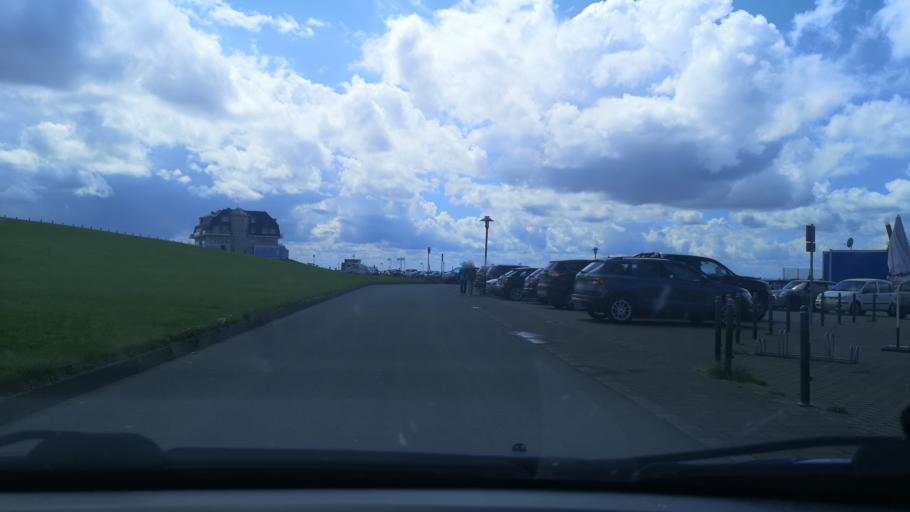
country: DE
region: Lower Saxony
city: Wremen
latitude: 53.6480
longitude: 8.4950
